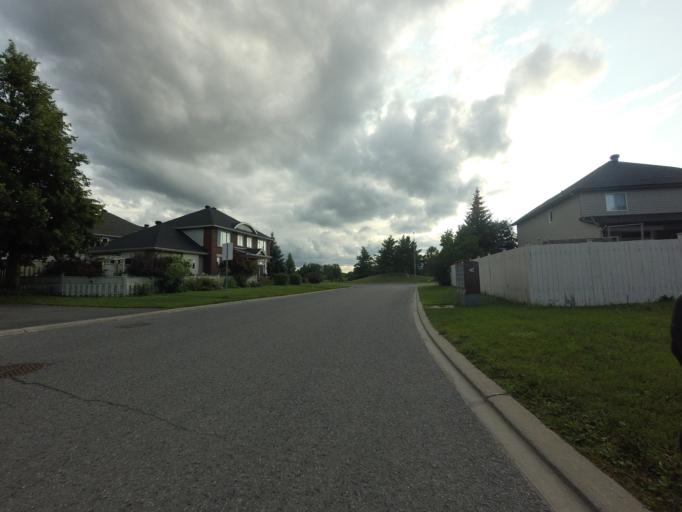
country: CA
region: Ontario
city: Bells Corners
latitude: 45.2877
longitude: -75.7142
